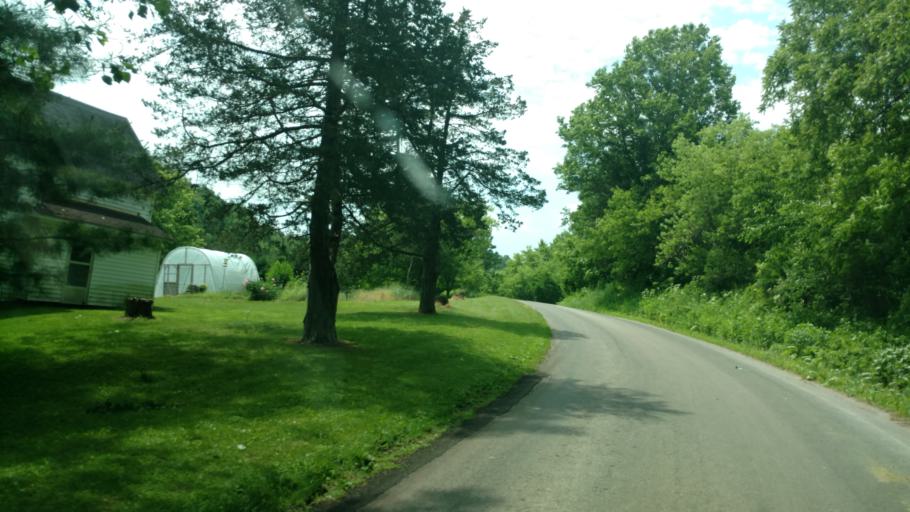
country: US
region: Wisconsin
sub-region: Monroe County
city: Cashton
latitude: 43.7215
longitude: -90.6753
